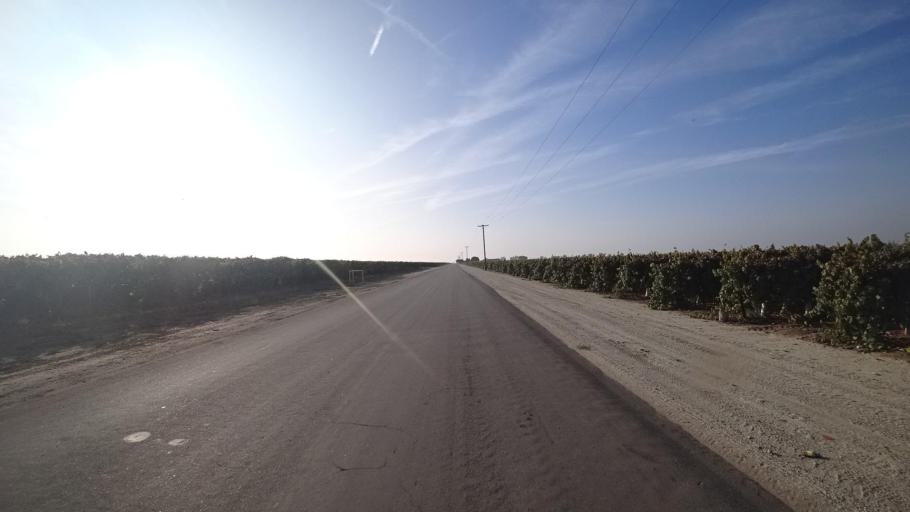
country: US
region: California
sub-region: Kern County
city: McFarland
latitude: 35.7030
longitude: -119.1871
